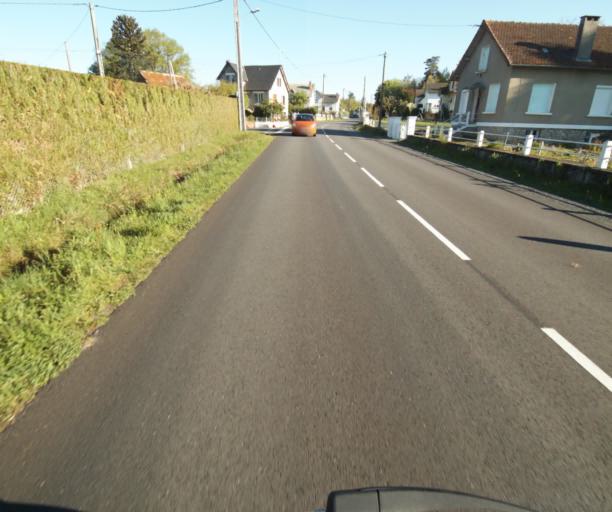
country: FR
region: Limousin
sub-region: Departement de la Correze
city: Correze
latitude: 45.3400
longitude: 1.8748
